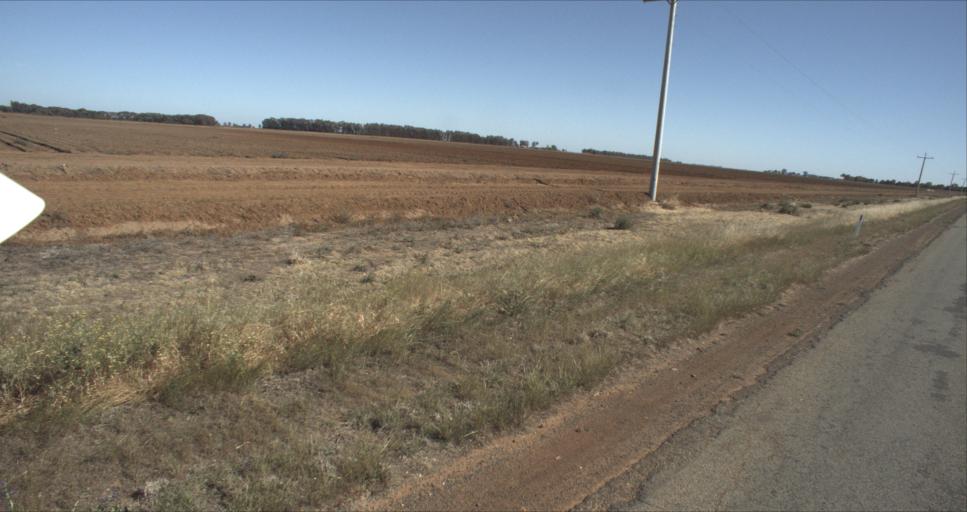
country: AU
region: New South Wales
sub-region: Leeton
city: Leeton
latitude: -34.6006
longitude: 146.2578
